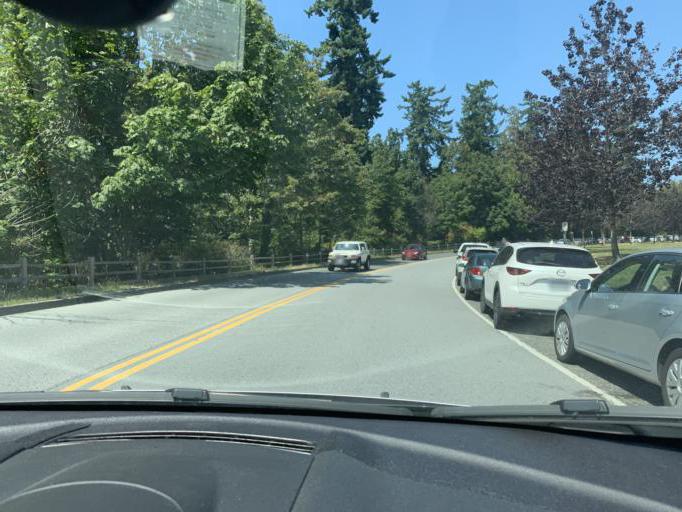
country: CA
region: British Columbia
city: West End
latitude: 49.2570
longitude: -123.2534
